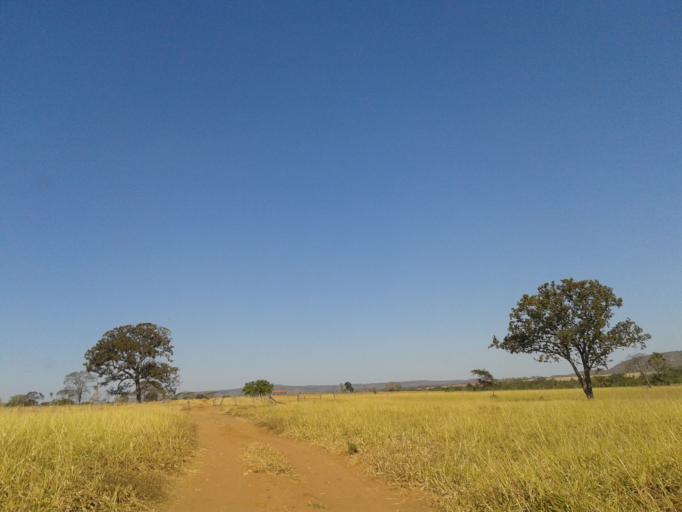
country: BR
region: Minas Gerais
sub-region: Santa Vitoria
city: Santa Vitoria
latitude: -19.1565
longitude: -50.0262
